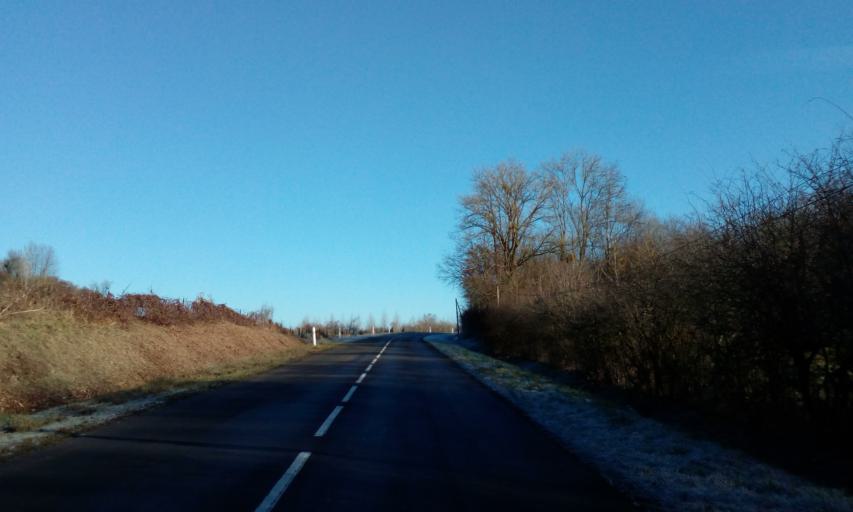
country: FR
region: Champagne-Ardenne
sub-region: Departement des Ardennes
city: Signy-le-Petit
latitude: 49.7582
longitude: 4.3212
